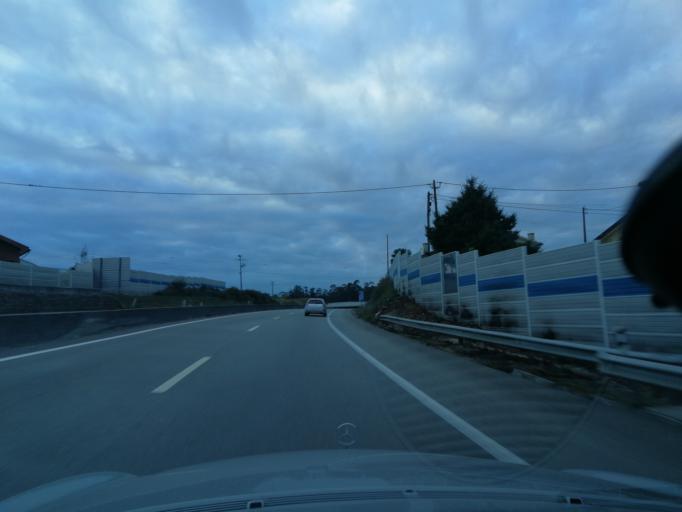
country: PT
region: Aveiro
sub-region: Albergaria-A-Velha
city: Albergaria-a-Velha
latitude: 40.6874
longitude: -8.5121
